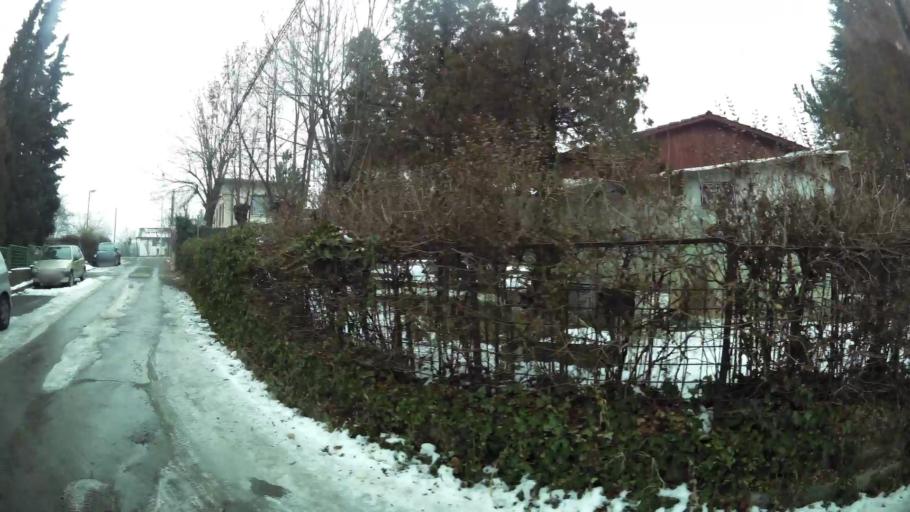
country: MK
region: Cair
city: Cair
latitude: 42.0138
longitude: 21.4580
